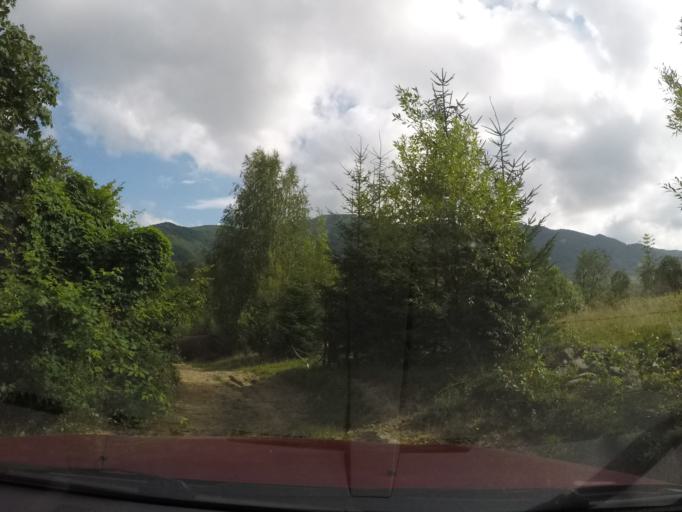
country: UA
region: Zakarpattia
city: Velykyi Bereznyi
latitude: 48.9441
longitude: 22.6846
